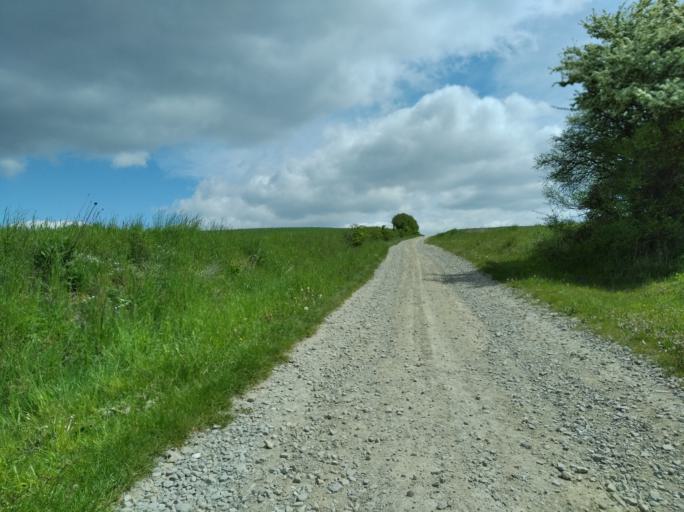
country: PL
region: Subcarpathian Voivodeship
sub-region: Powiat strzyzowski
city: Frysztak
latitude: 49.8945
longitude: 21.5652
